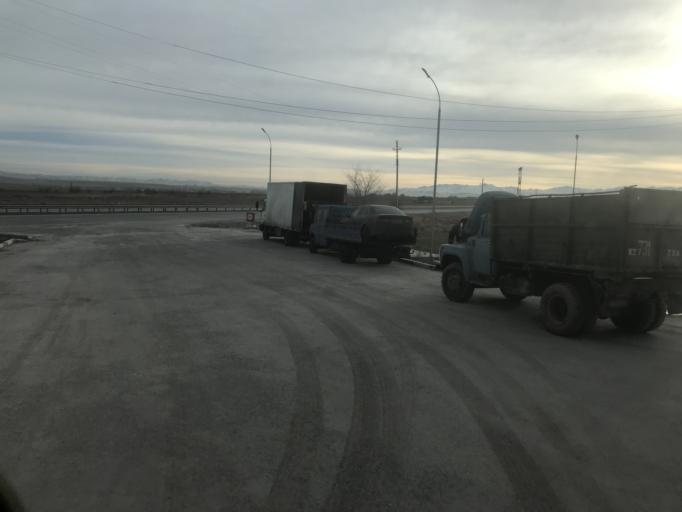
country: KZ
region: Ongtustik Qazaqstan
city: Shymkent
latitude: 42.4623
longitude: 69.5757
